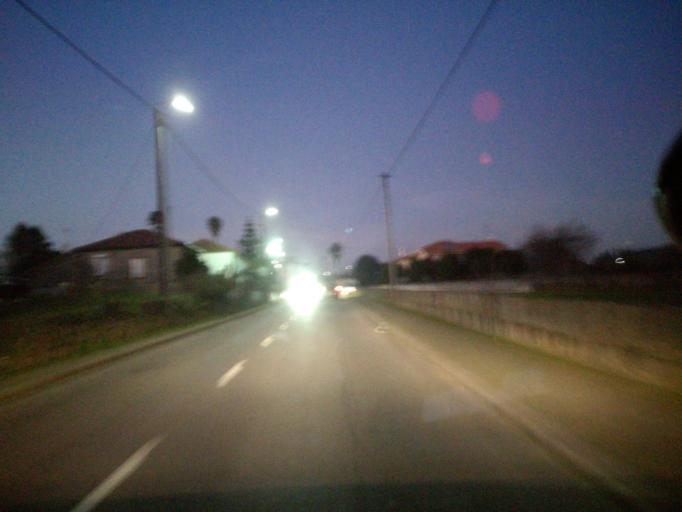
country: PT
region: Porto
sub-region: Maia
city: Nogueira
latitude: 41.2497
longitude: -8.5840
